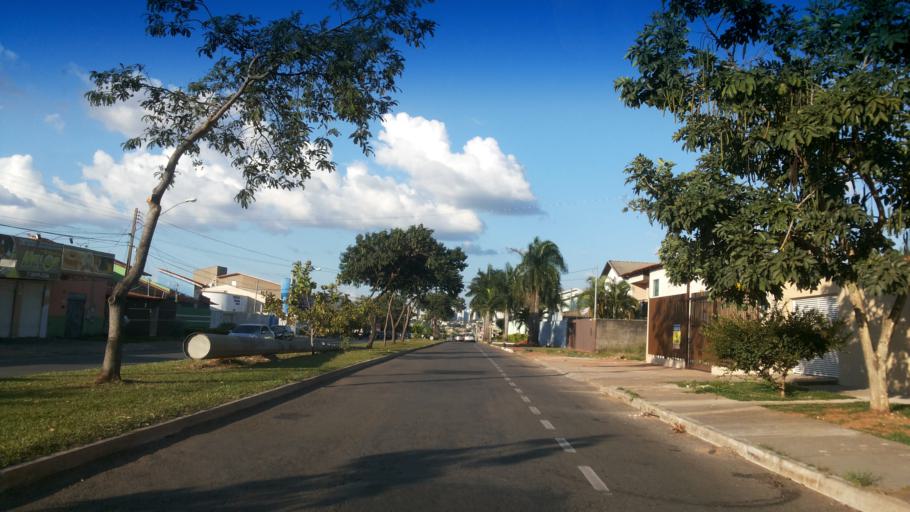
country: BR
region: Goias
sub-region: Goiania
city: Goiania
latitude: -16.7270
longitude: -49.3047
